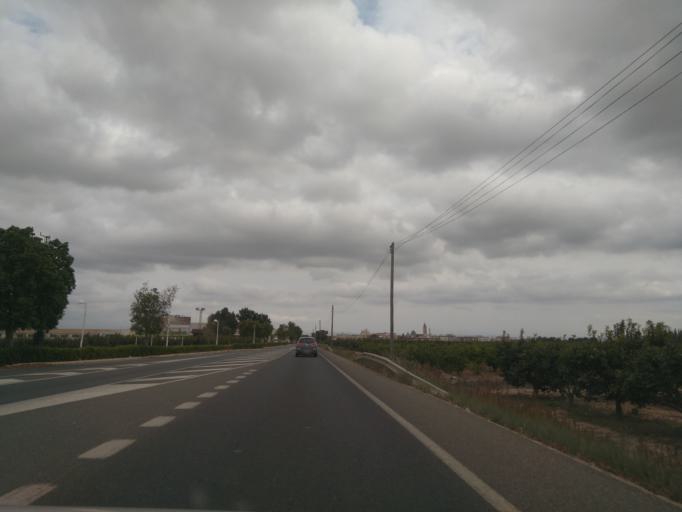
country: ES
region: Valencia
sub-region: Provincia de Valencia
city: L'Alcudia
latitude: 39.2085
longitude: -0.5105
